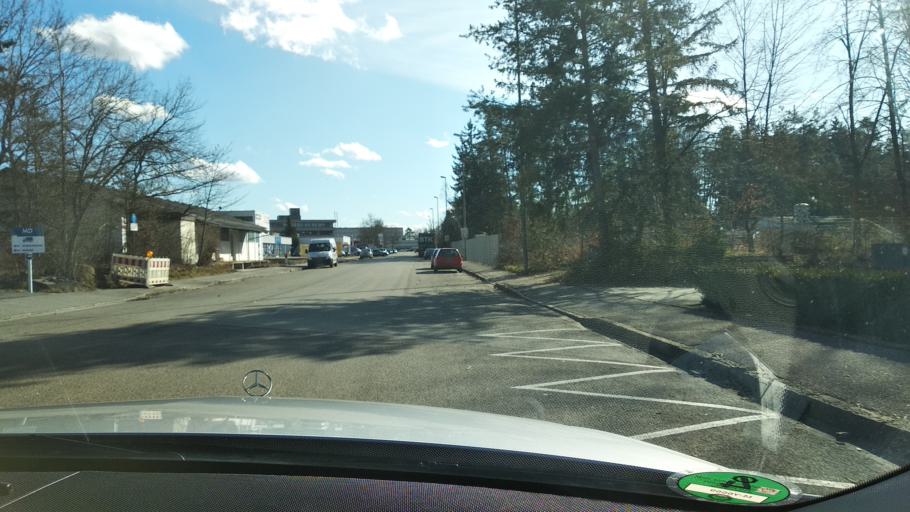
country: DE
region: Bavaria
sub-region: Upper Bavaria
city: Waldkraiburg
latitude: 48.2124
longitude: 12.4124
